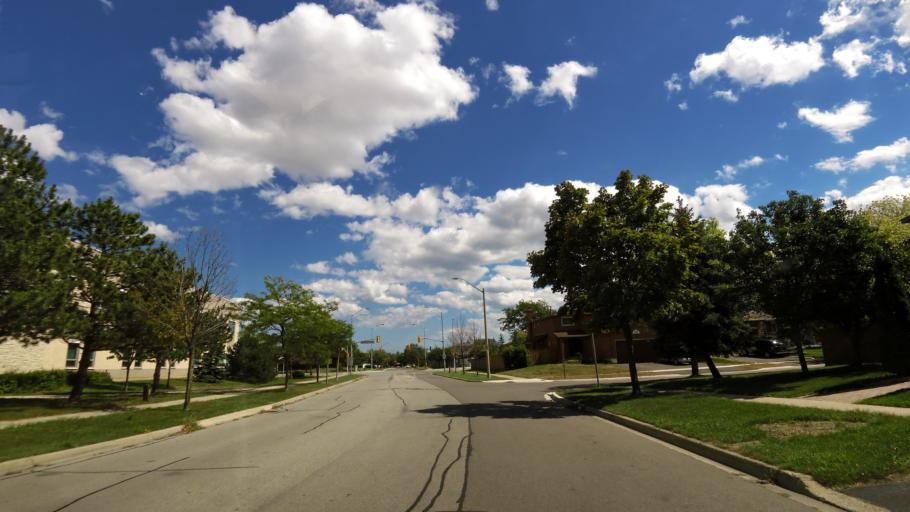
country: CA
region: Ontario
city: Mississauga
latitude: 43.6124
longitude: -79.6215
